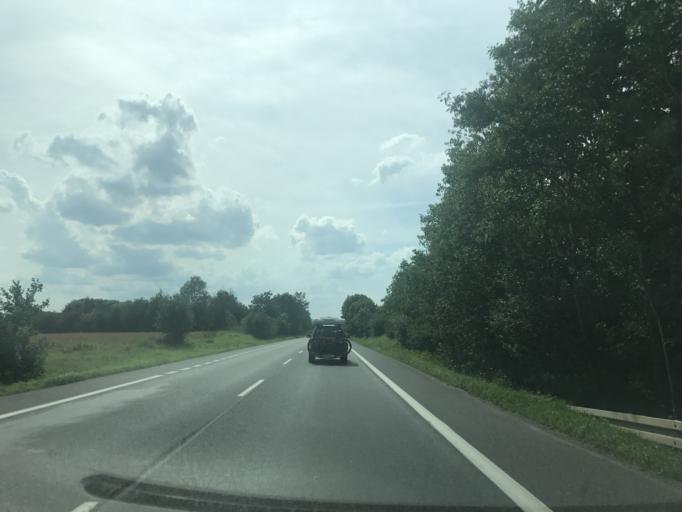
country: PL
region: Masovian Voivodeship
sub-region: Powiat mlawski
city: Mlawa
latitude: 53.1000
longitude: 20.3913
